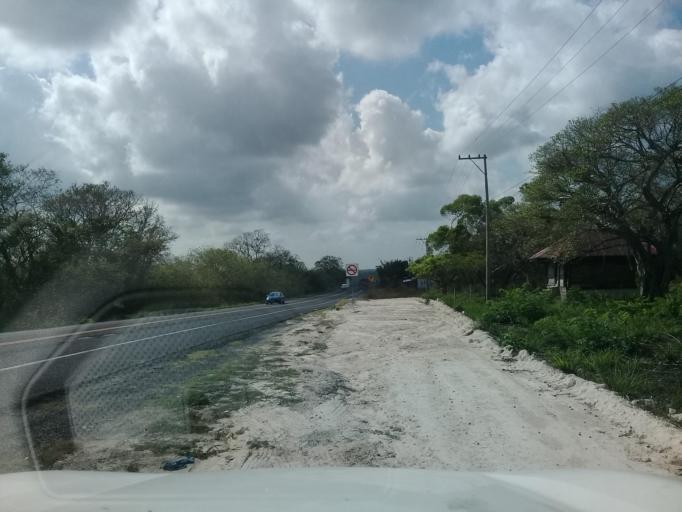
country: MX
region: Veracruz
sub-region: Emiliano Zapata
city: Plan del Rio
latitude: 19.4116
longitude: -96.6513
